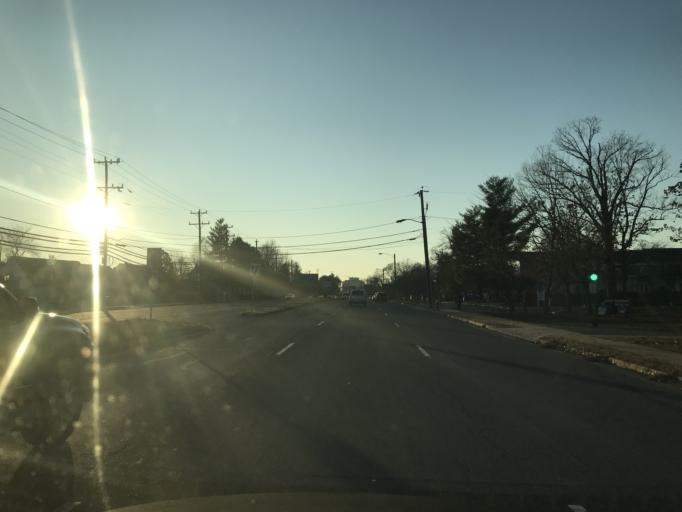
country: US
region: Virginia
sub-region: Fairfax County
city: Franconia
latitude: 38.7787
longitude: -77.1646
